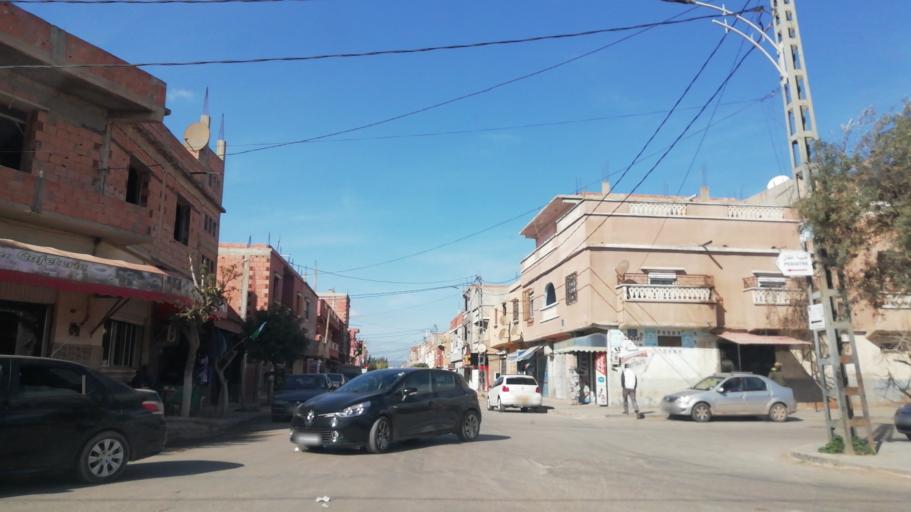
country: DZ
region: Oran
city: Es Senia
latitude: 35.6134
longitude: -0.5776
